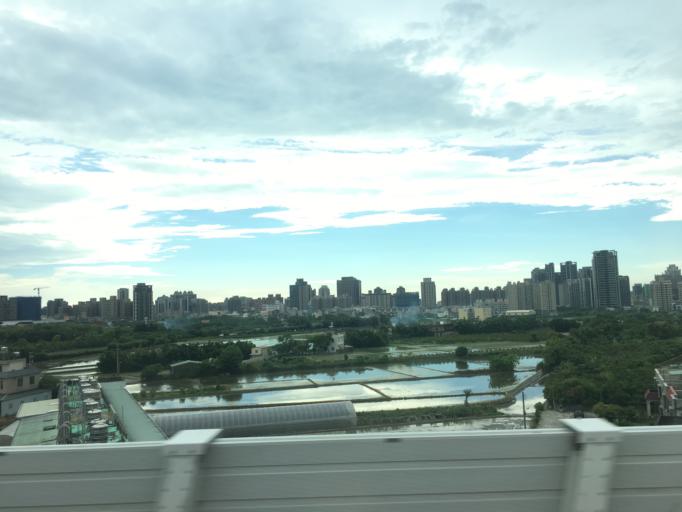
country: TW
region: Taiwan
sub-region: Hsinchu
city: Zhubei
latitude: 24.8171
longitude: 121.0425
